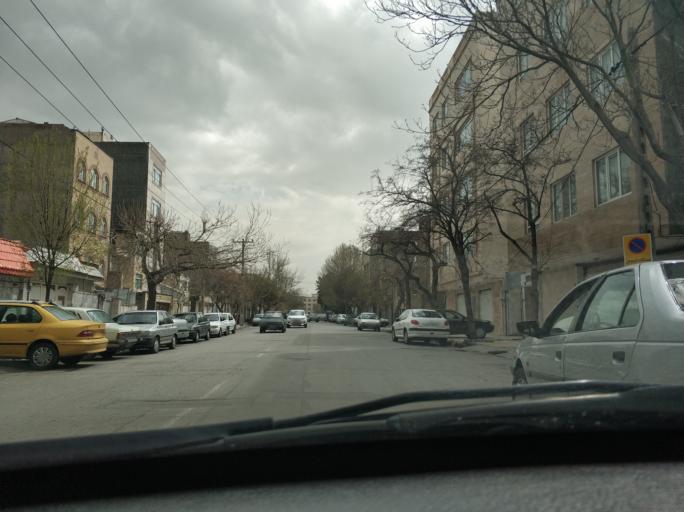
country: IR
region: Razavi Khorasan
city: Mashhad
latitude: 36.2751
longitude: 59.5724
